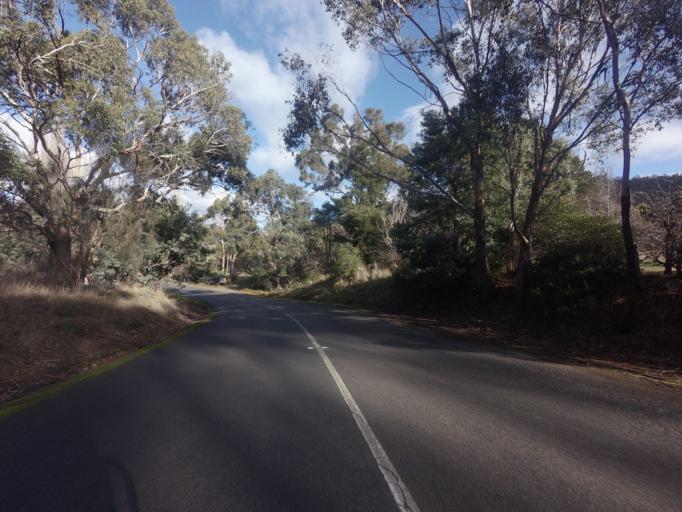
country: AU
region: Tasmania
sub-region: Derwent Valley
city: New Norfolk
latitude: -42.7923
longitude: 147.1224
